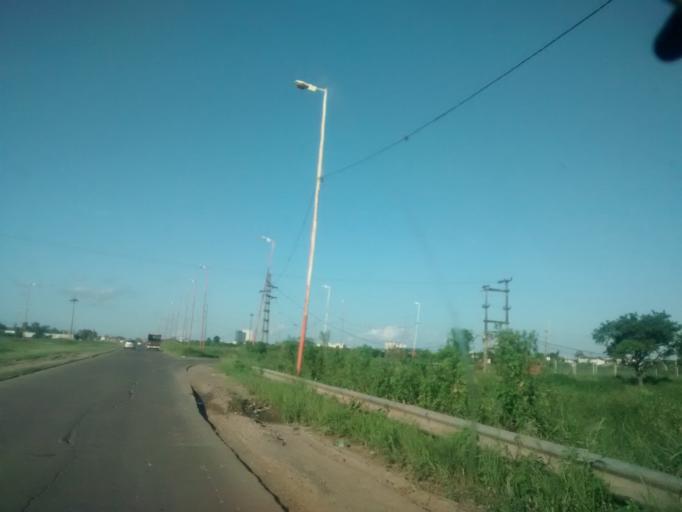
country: AR
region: Chaco
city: Fontana
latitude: -27.4524
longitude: -59.0301
